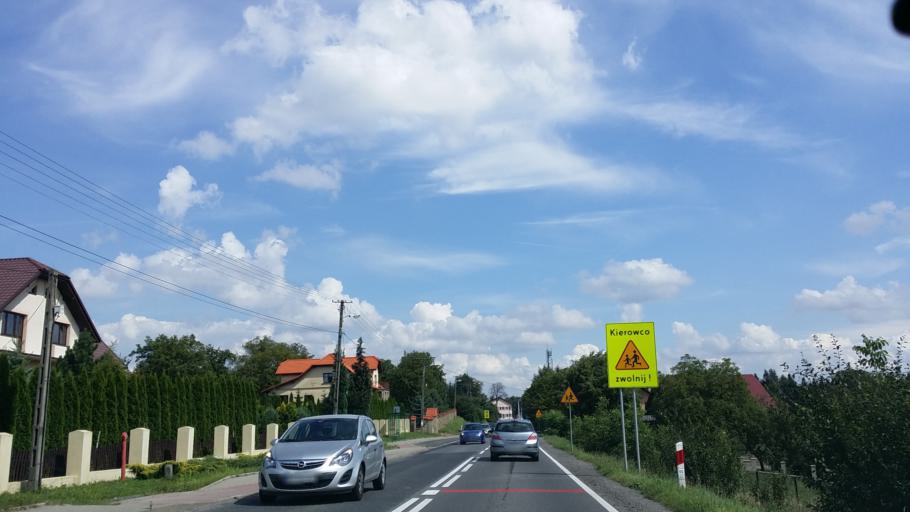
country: PL
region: Lesser Poland Voivodeship
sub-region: Powiat wielicki
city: Pawlikowice
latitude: 49.9361
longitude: 20.0586
